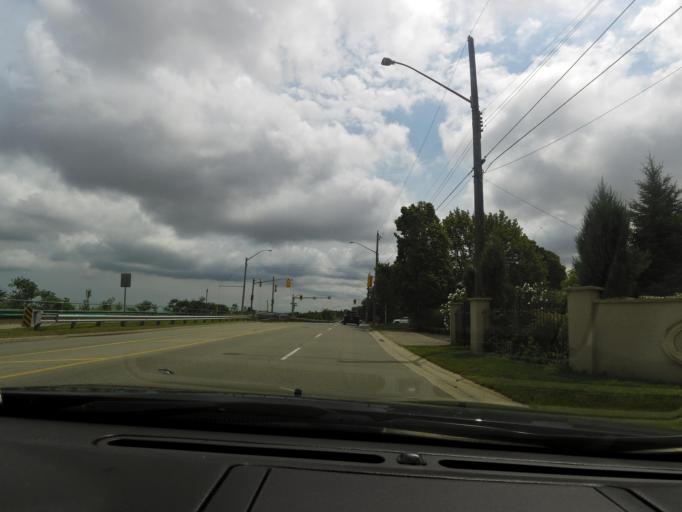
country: CA
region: Ontario
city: Hamilton
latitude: 43.2330
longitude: -79.8271
